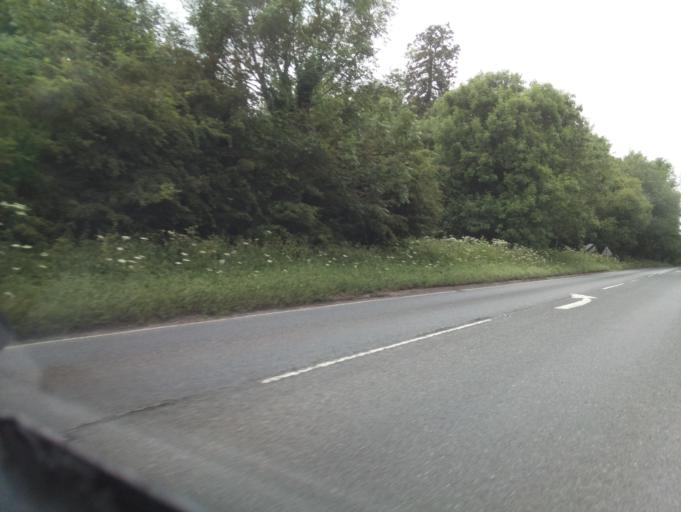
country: GB
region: England
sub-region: Staffordshire
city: Mayfield
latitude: 52.9888
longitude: -1.7471
